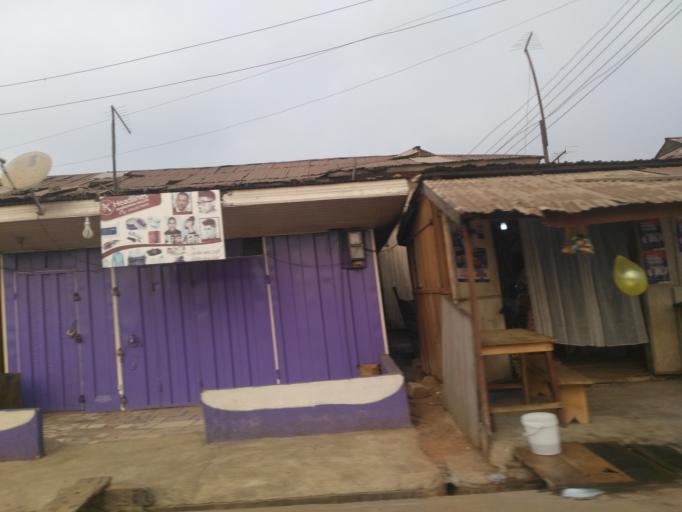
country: GH
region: Ashanti
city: Kumasi
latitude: 6.6833
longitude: -1.5906
